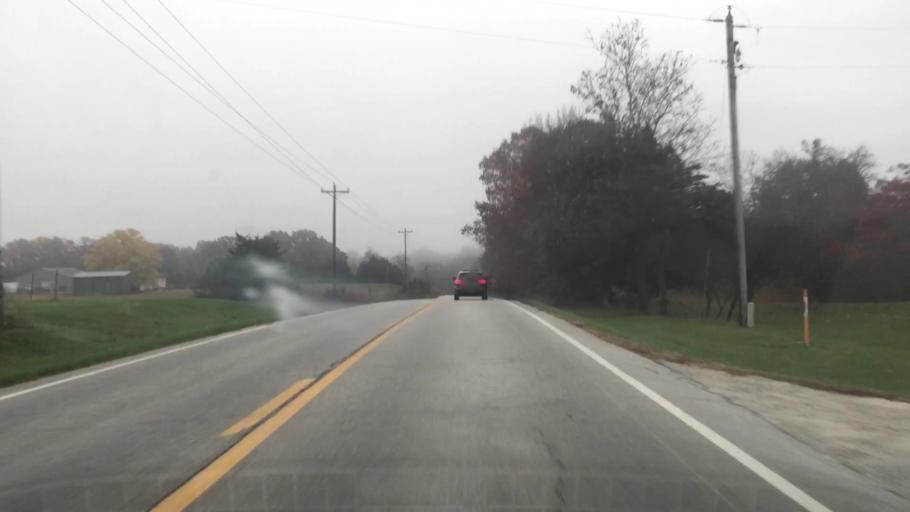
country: US
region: Missouri
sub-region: Callaway County
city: Fulton
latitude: 38.8737
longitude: -92.0450
